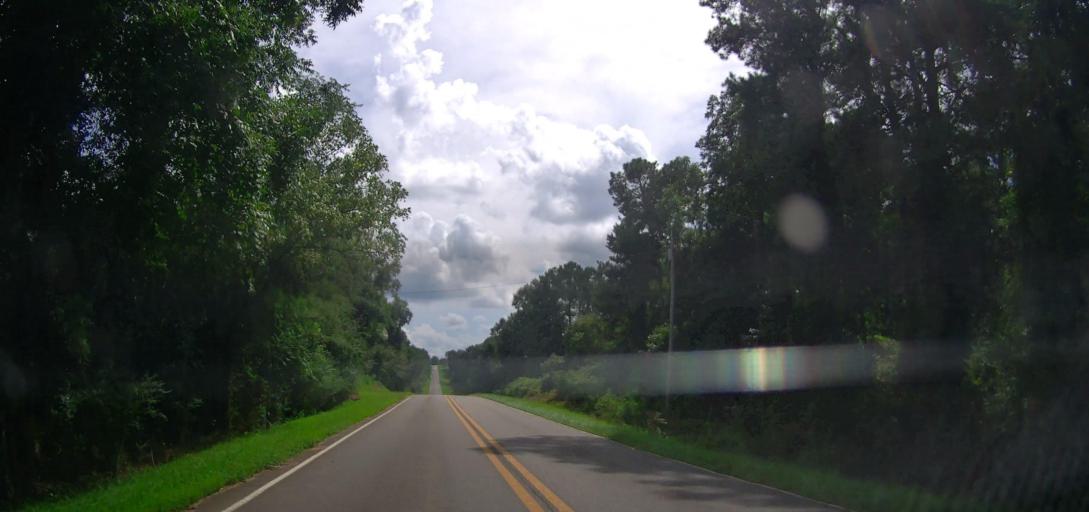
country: US
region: Georgia
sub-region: Taylor County
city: Butler
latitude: 32.4874
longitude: -84.2057
